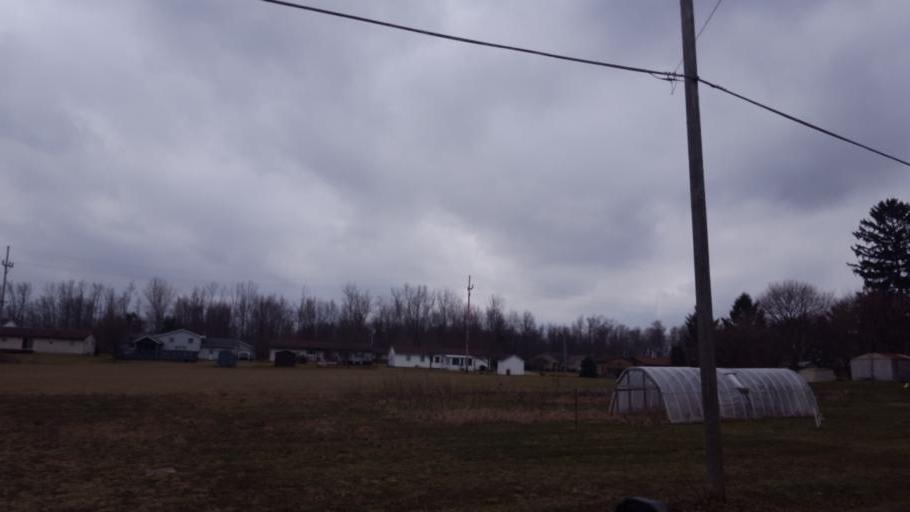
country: US
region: Ohio
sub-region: Richland County
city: Shelby
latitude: 40.8799
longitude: -82.6840
